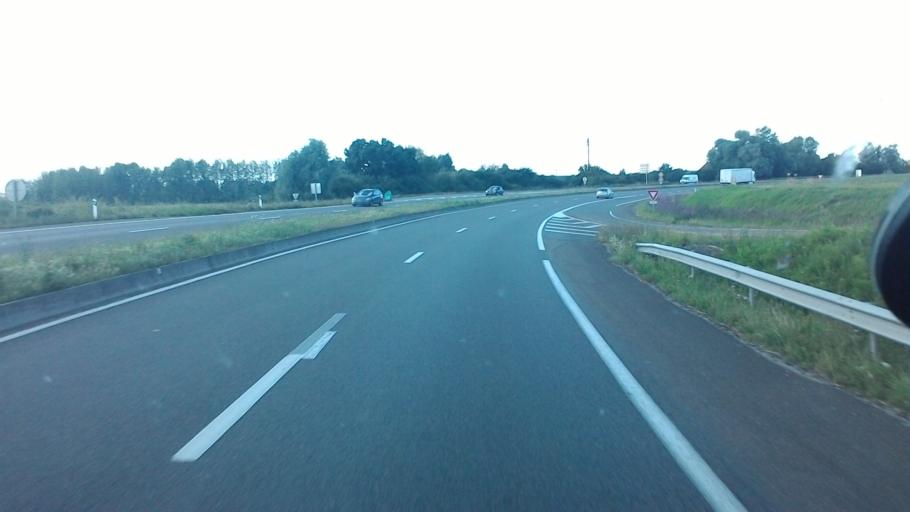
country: FR
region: Franche-Comte
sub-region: Departement de la Haute-Saone
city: Pusey
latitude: 47.6356
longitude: 6.1355
